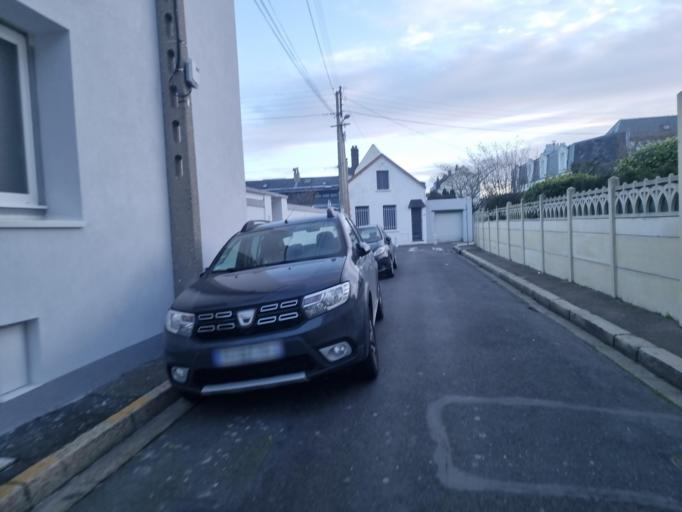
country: FR
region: Haute-Normandie
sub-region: Departement de la Seine-Maritime
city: Le Havre
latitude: 49.5074
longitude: 0.1036
